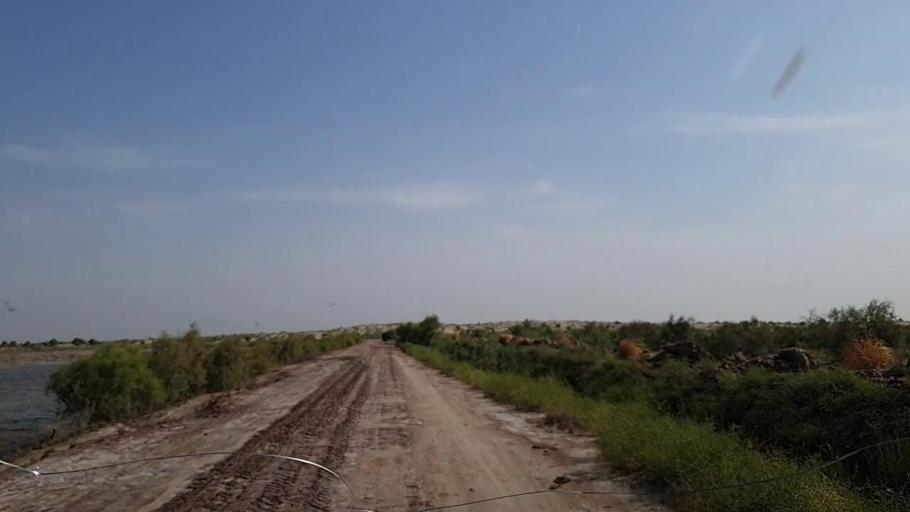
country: PK
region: Sindh
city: Khanpur
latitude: 27.6777
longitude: 69.3683
